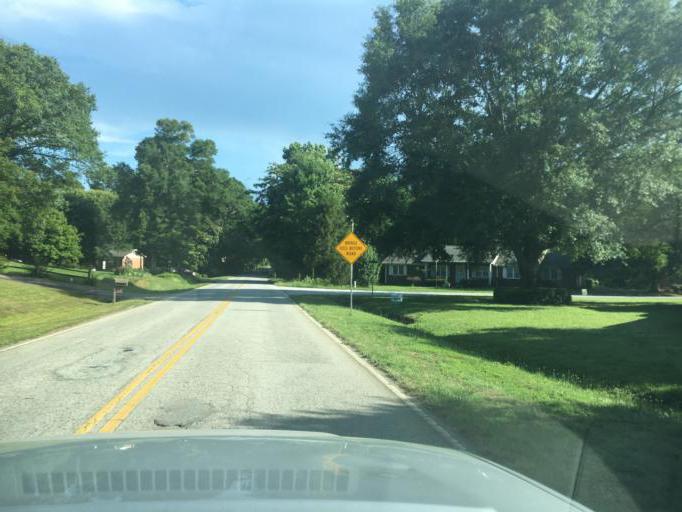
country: US
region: South Carolina
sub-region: Greenville County
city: Mauldin
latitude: 34.7884
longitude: -82.2979
